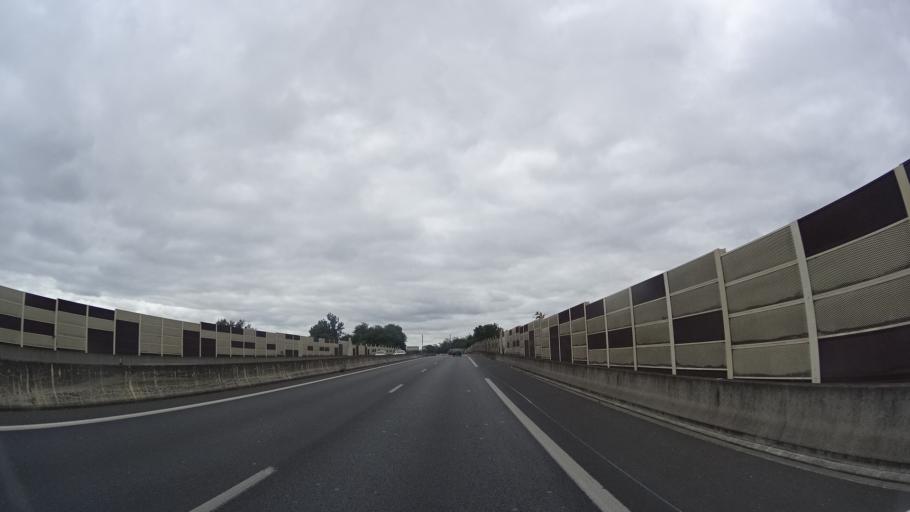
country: FR
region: Pays de la Loire
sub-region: Departement de Maine-et-Loire
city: Les Ponts-de-Ce
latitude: 47.4507
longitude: -0.5150
